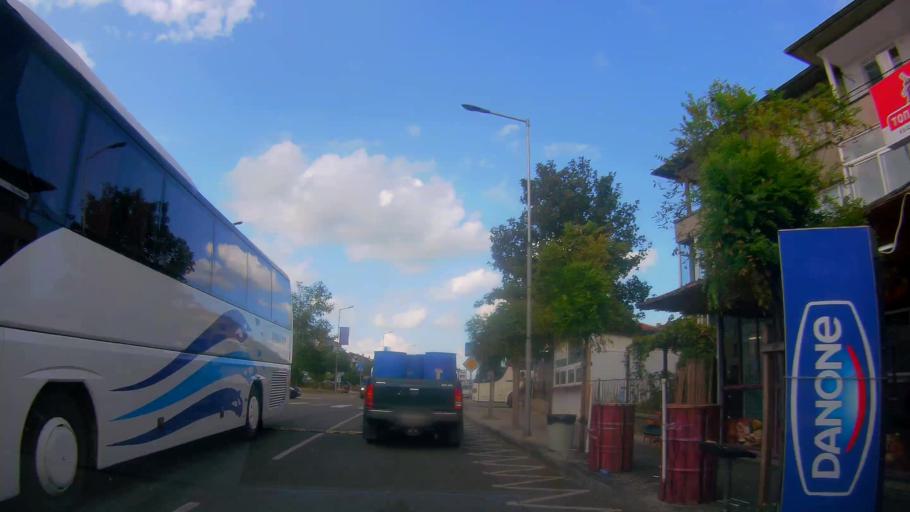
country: BG
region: Burgas
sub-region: Obshtina Primorsko
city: Primorsko
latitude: 42.2679
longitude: 27.7495
